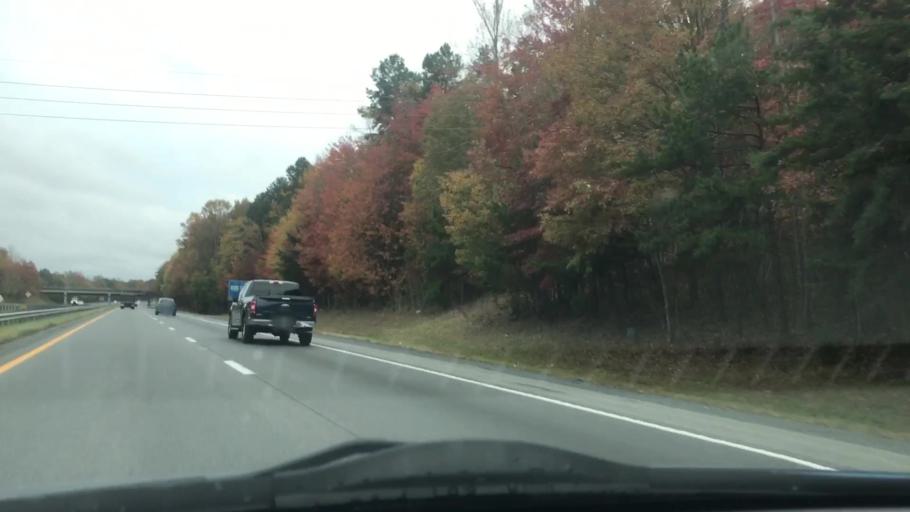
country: US
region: North Carolina
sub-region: Randolph County
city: Asheboro
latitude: 35.7357
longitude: -79.8249
